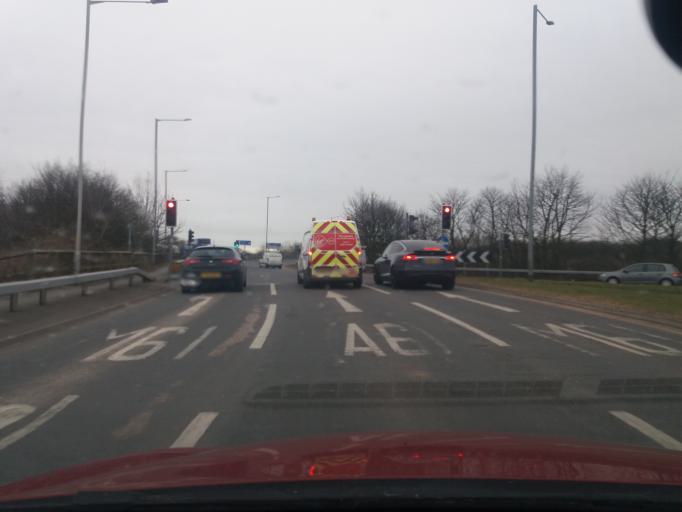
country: GB
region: England
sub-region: Lancashire
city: Chorley
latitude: 53.6709
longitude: -2.6234
